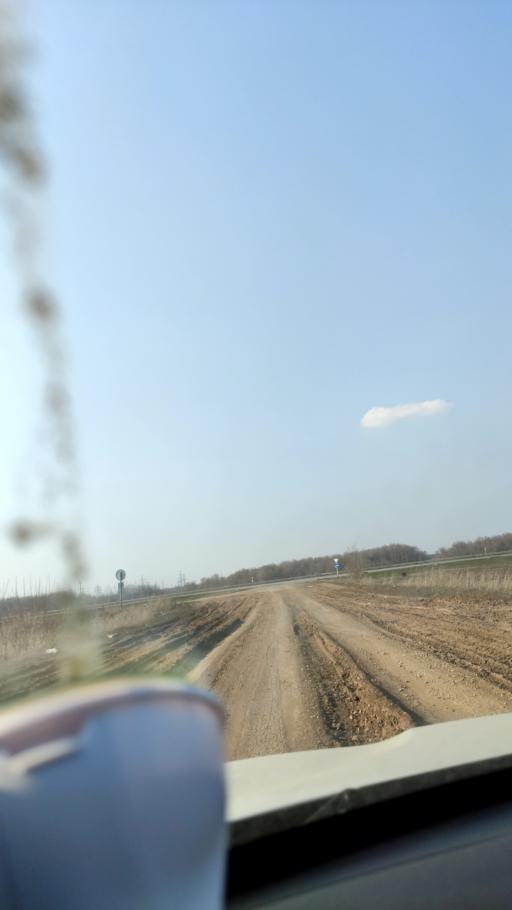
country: RU
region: Samara
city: Kinel'
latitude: 53.2609
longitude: 50.5257
